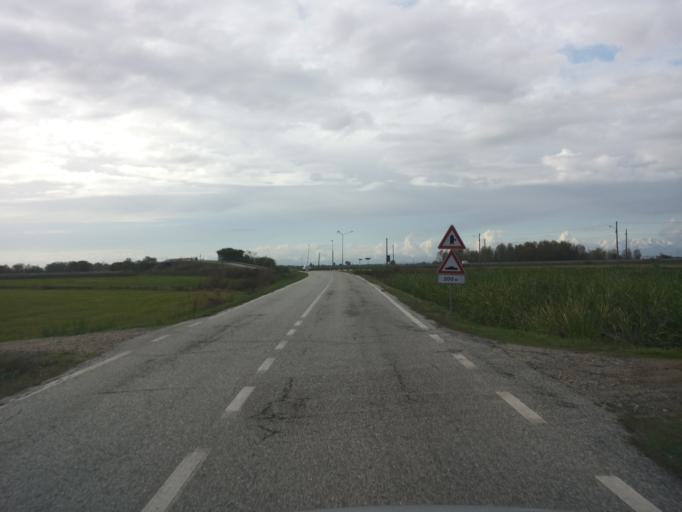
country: IT
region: Piedmont
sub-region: Provincia di Vercelli
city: Pezzana
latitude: 45.2592
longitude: 8.4731
